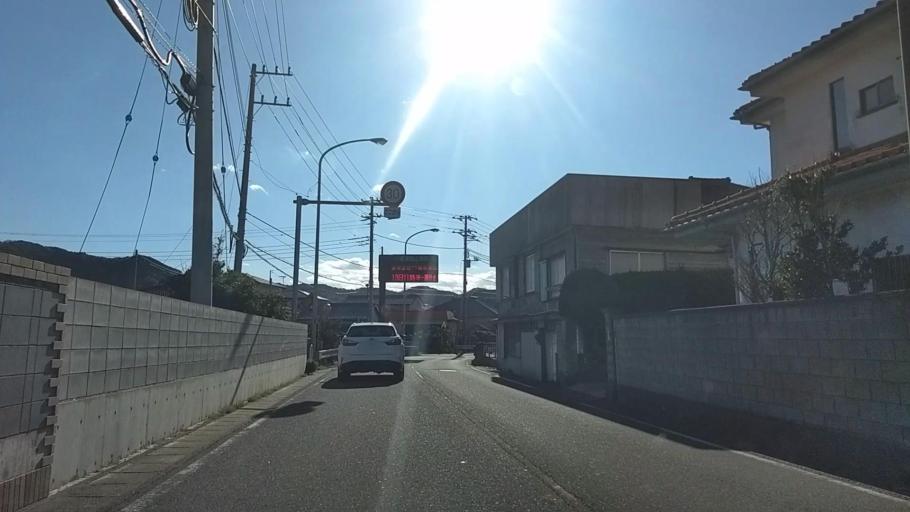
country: JP
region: Chiba
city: Futtsu
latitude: 35.1435
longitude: 139.8352
